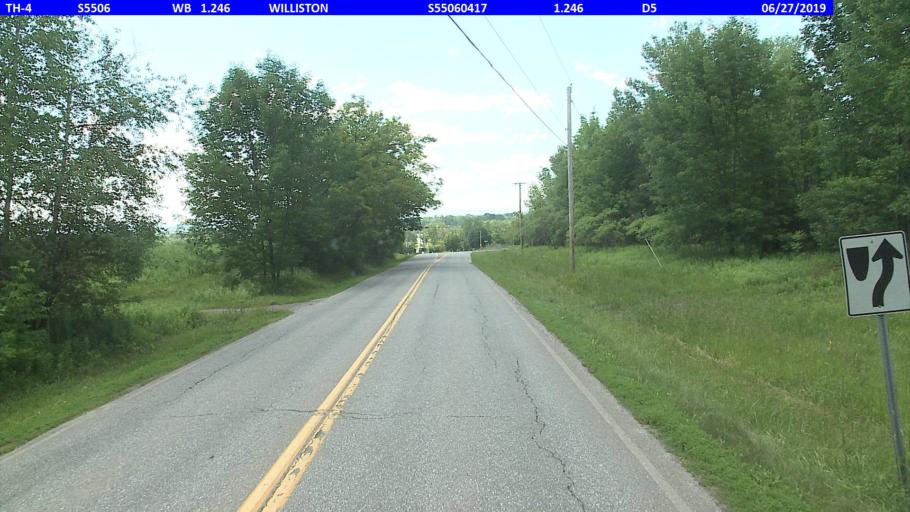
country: US
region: Vermont
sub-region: Chittenden County
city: Williston
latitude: 44.4608
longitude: -73.0900
